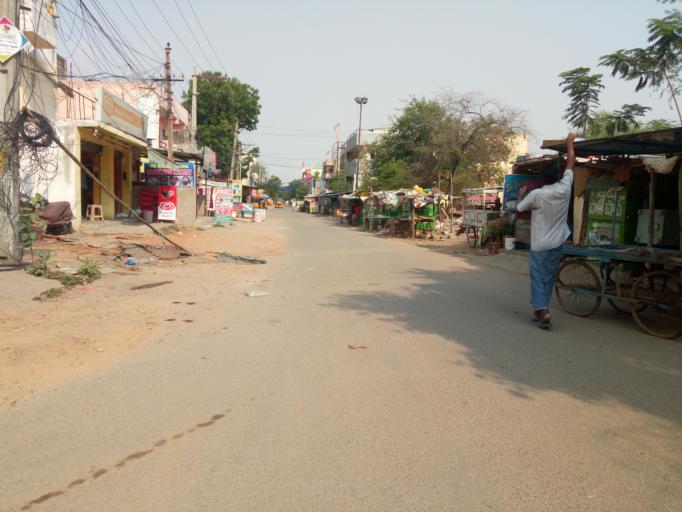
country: IN
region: Telangana
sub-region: Rangareddi
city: Kukatpalli
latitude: 17.4721
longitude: 78.3886
